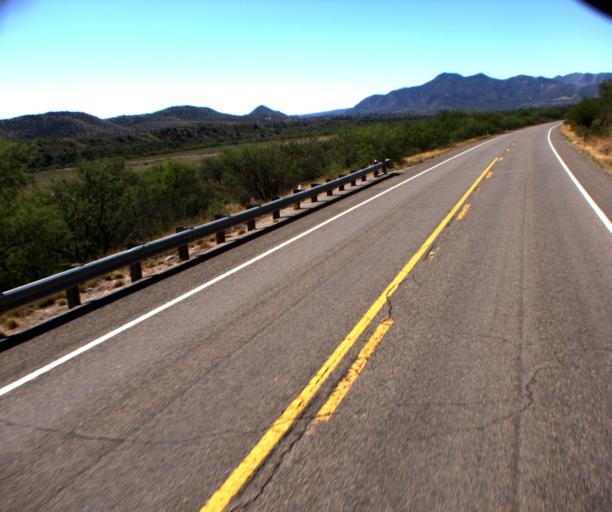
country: US
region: Arizona
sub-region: Santa Cruz County
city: Rio Rico
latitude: 31.6016
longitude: -110.7225
